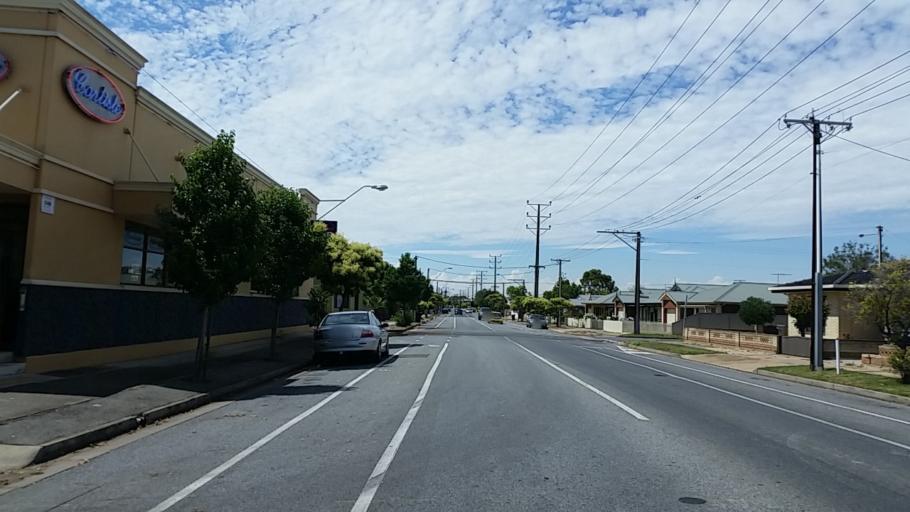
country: AU
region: South Australia
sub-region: Charles Sturt
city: West Lakes Shore
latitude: -34.8496
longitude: 138.4899
